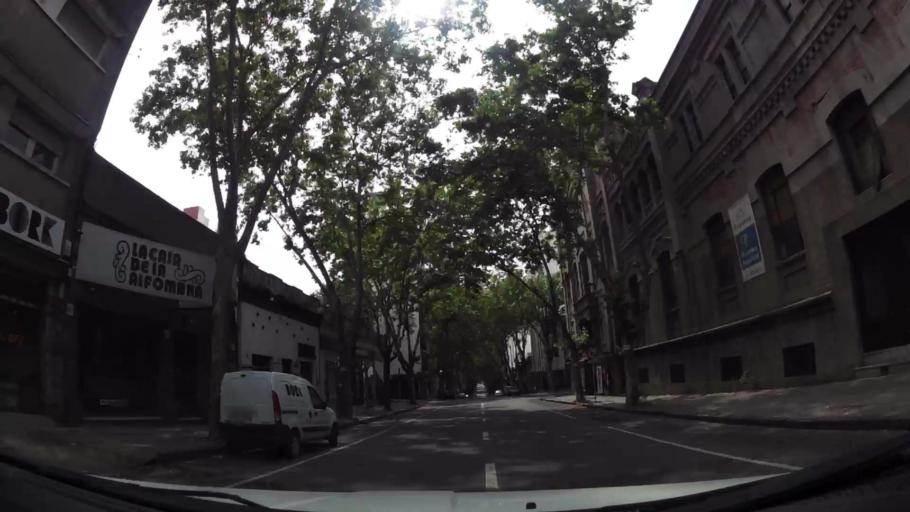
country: UY
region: Montevideo
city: Montevideo
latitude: -34.9072
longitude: -56.1691
